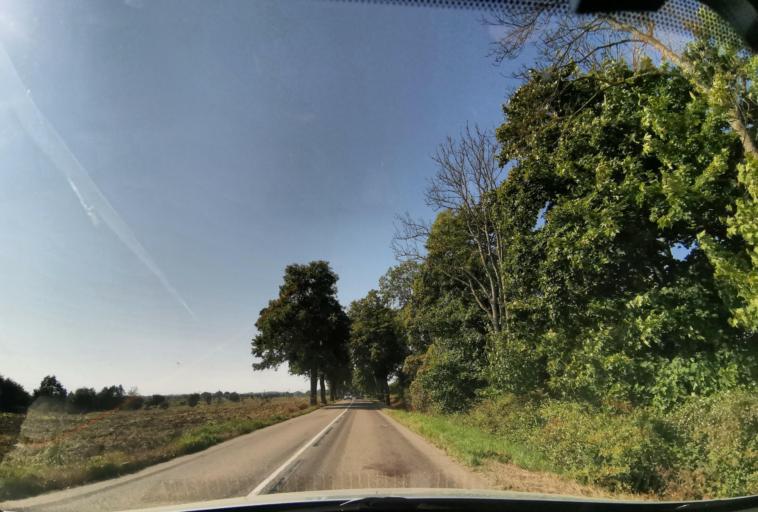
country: RU
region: Kaliningrad
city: Primorsk
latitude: 54.8014
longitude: 20.0502
